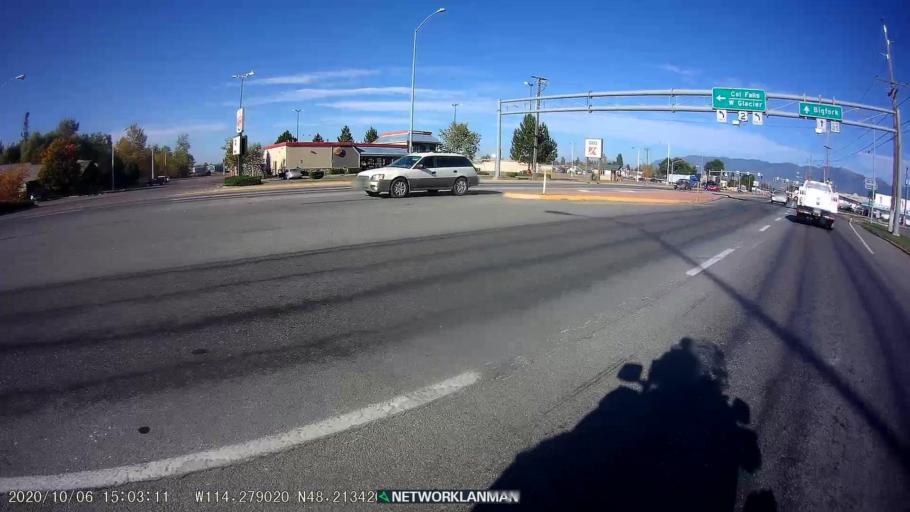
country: US
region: Montana
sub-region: Flathead County
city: Evergreen
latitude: 48.2136
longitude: -114.2782
